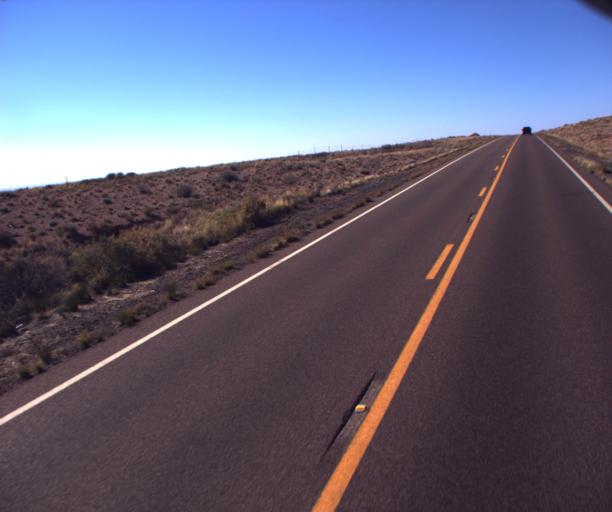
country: US
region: Arizona
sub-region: Navajo County
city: Joseph City
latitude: 35.1612
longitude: -110.4581
